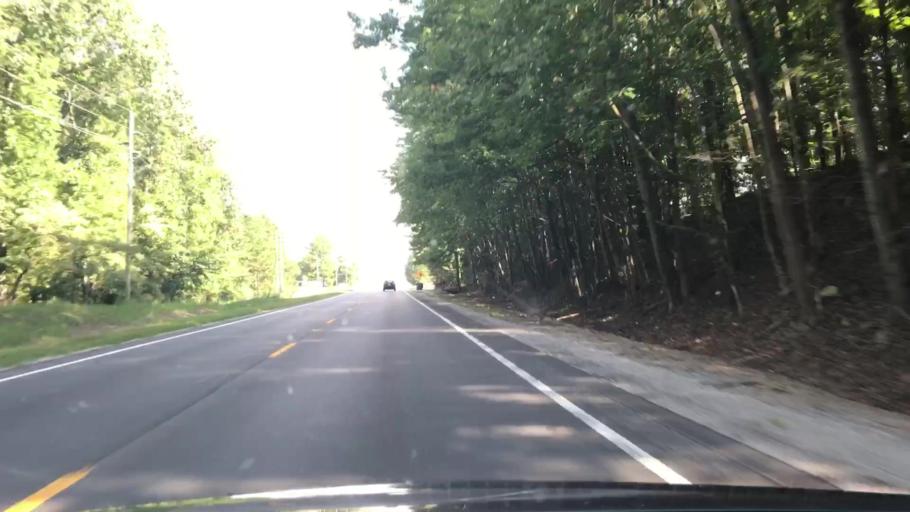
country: US
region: Alabama
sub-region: Madison County
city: Harvest
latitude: 34.9167
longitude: -86.7621
